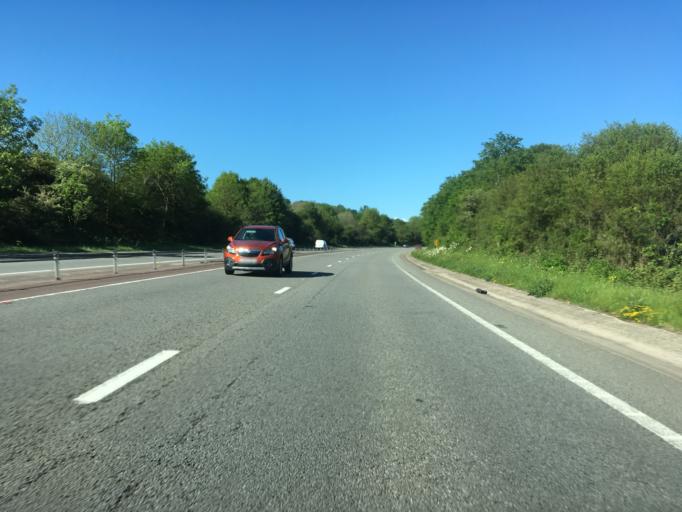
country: GB
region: Wales
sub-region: Monmouthshire
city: Mitchel Troy
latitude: 51.7743
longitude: -2.8019
